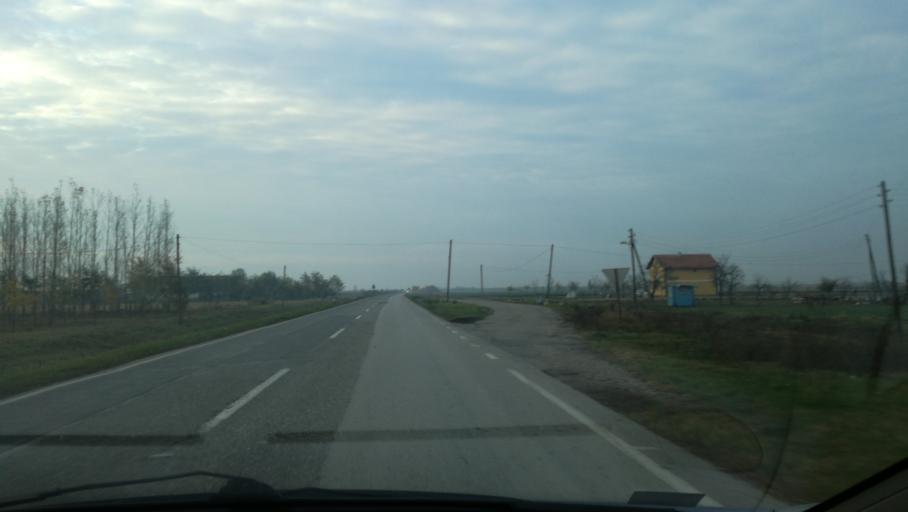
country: RS
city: Basaid
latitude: 45.6773
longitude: 20.4227
